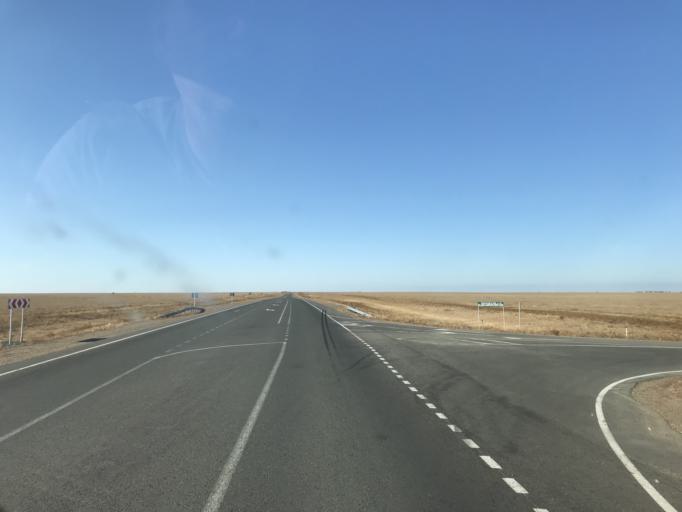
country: KZ
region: Pavlodar
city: Kurchatov
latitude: 51.2159
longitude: 78.6402
